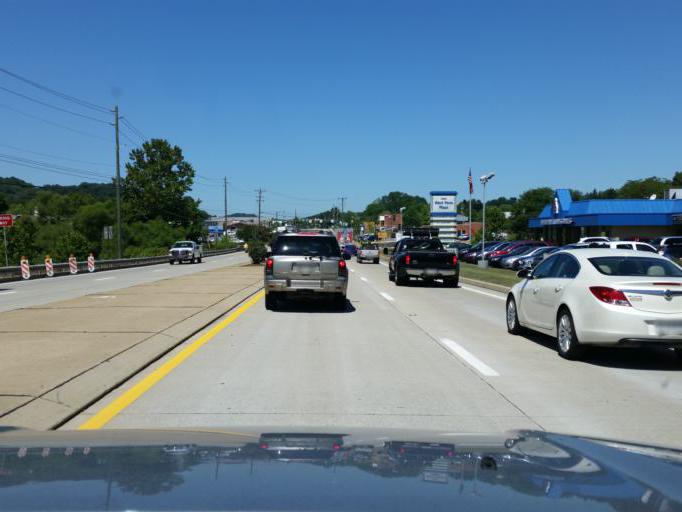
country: US
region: Pennsylvania
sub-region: Westmoreland County
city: Murrysville
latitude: 40.4214
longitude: -79.6585
